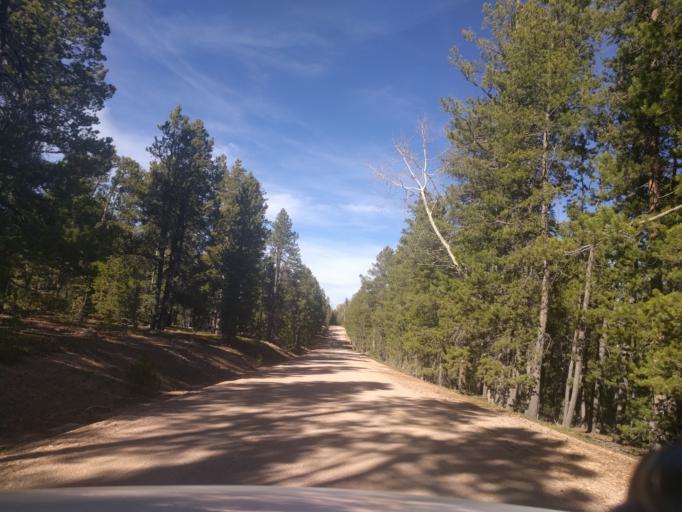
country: US
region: Colorado
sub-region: Douglas County
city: Perry Park
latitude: 39.1938
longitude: -105.0519
